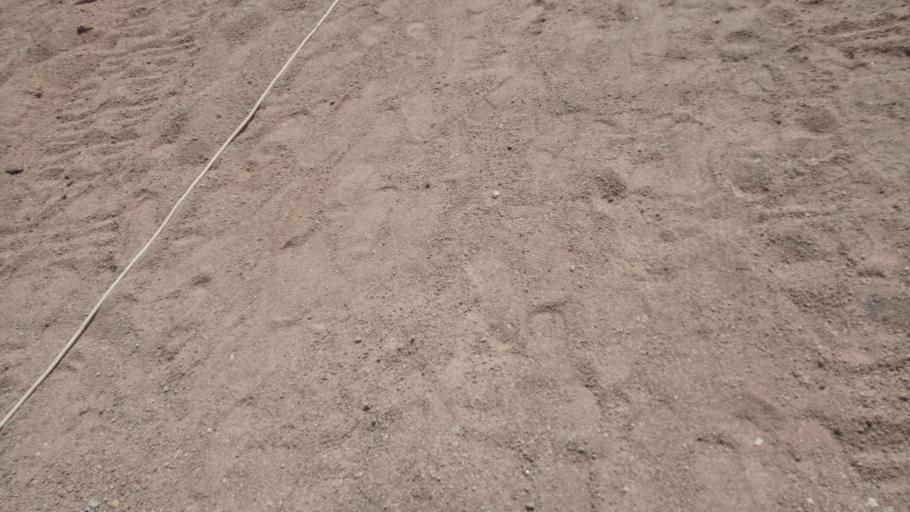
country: NG
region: Adamawa
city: Mayo Belwa
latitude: 9.1576
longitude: 12.0154
